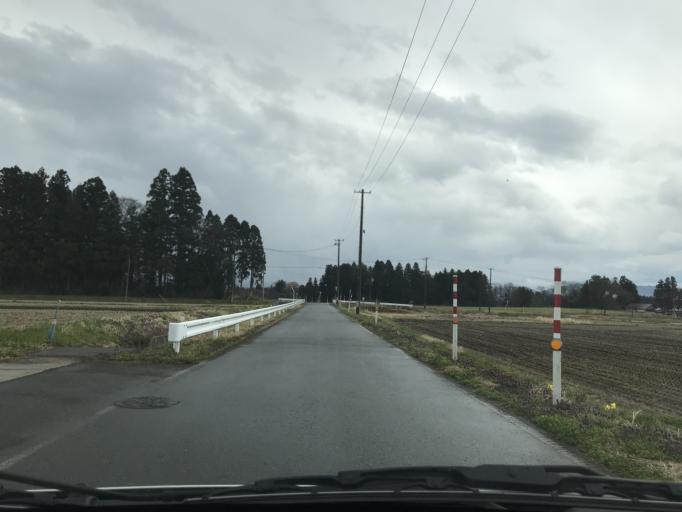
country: JP
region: Iwate
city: Mizusawa
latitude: 39.0956
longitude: 141.0886
